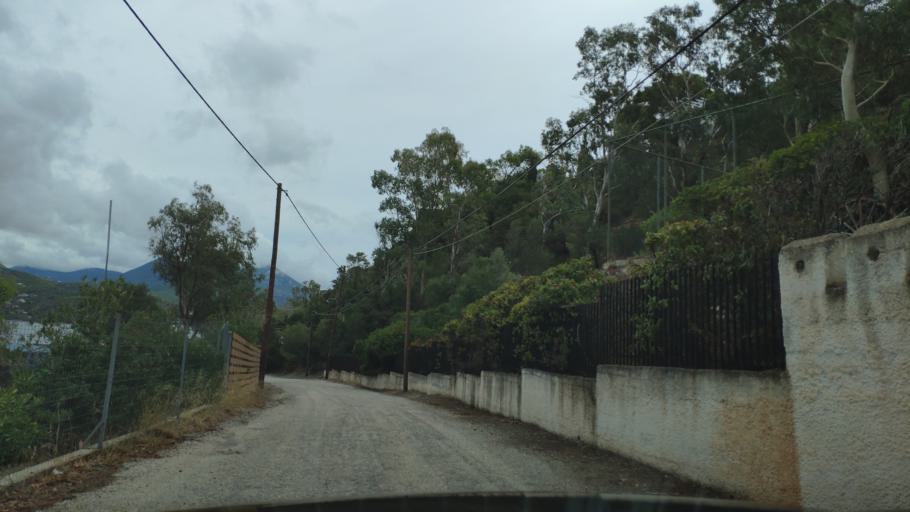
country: GR
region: Peloponnese
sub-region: Nomos Korinthias
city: Perachora
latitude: 38.0264
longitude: 22.8724
